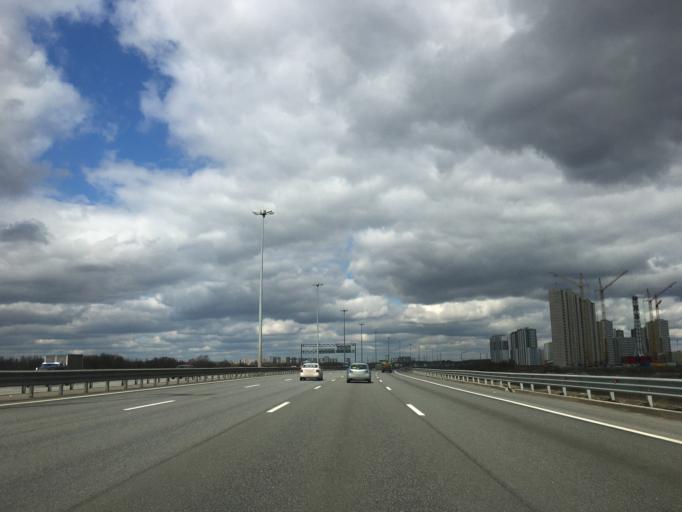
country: RU
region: St.-Petersburg
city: Krasnogvargeisky
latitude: 59.9976
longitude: 30.4773
